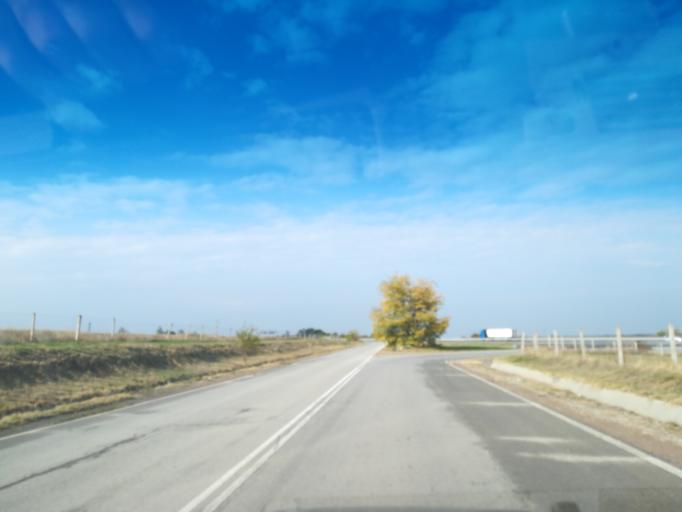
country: BG
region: Stara Zagora
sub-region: Obshtina Chirpan
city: Chirpan
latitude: 42.2064
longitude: 25.3021
